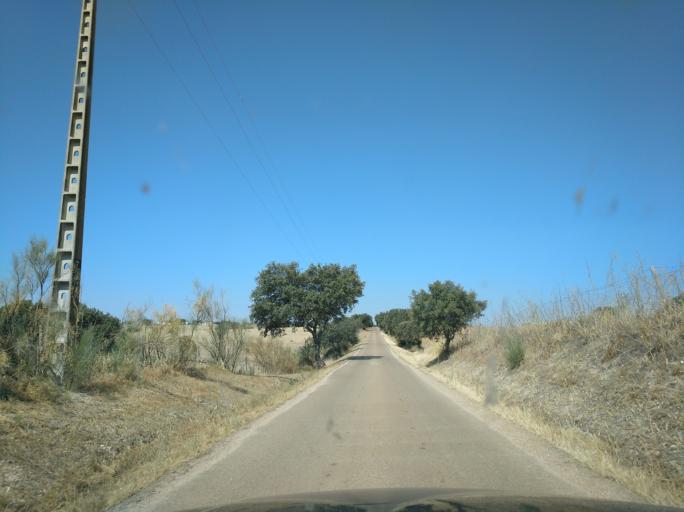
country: PT
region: Portalegre
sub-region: Campo Maior
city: Campo Maior
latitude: 39.0461
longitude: -7.0067
